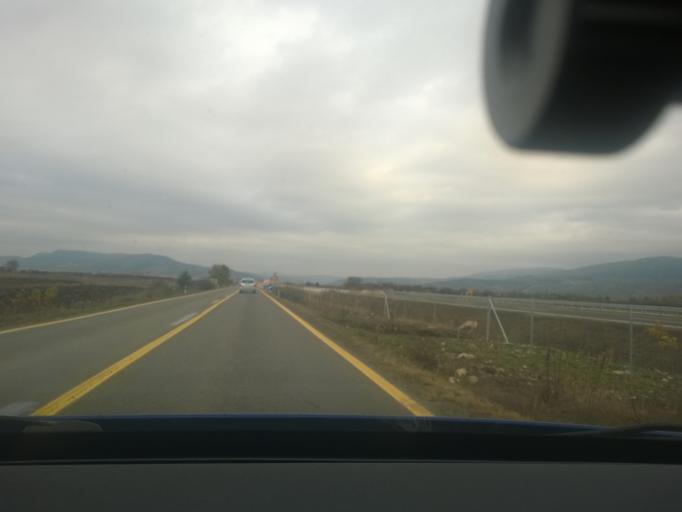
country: RS
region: Central Serbia
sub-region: Pirotski Okrug
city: Pirot
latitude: 43.1143
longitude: 22.6282
